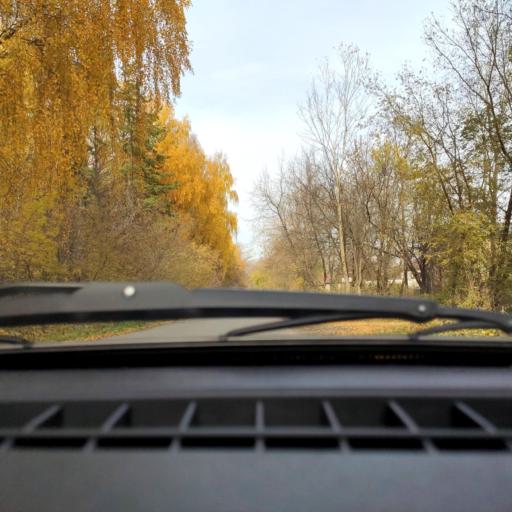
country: RU
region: Bashkortostan
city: Ufa
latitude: 54.7894
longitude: 56.1586
